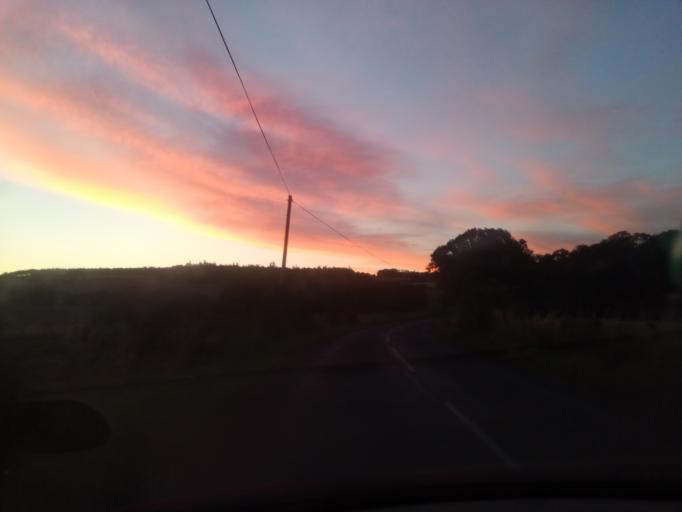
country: GB
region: England
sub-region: Northumberland
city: Wall
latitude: 55.0187
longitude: -2.1499
